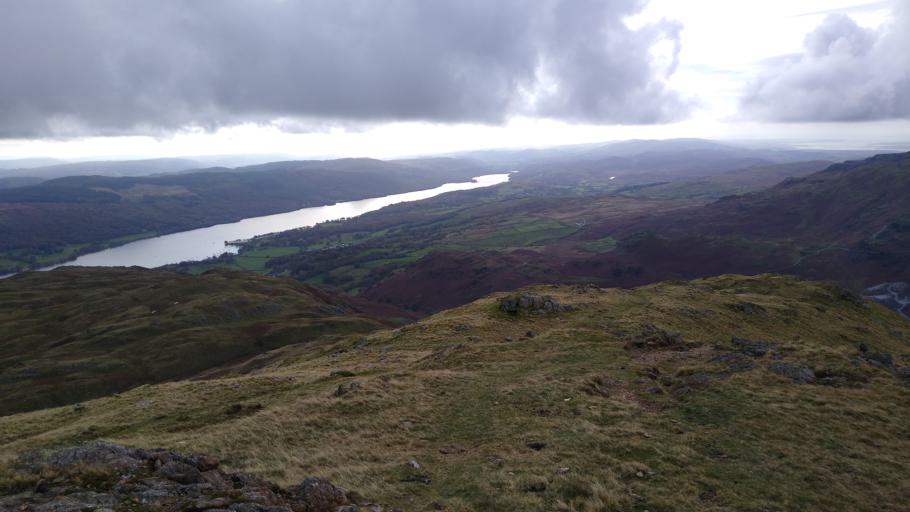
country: GB
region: England
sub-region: Cumbria
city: Ambleside
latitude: 54.3884
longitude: -3.0922
